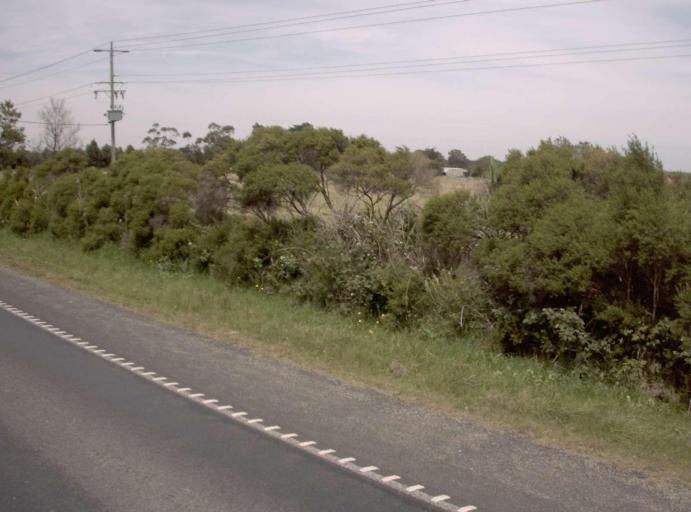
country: AU
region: Victoria
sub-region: Mornington Peninsula
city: Langwarrin South
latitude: -38.2215
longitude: 145.2182
